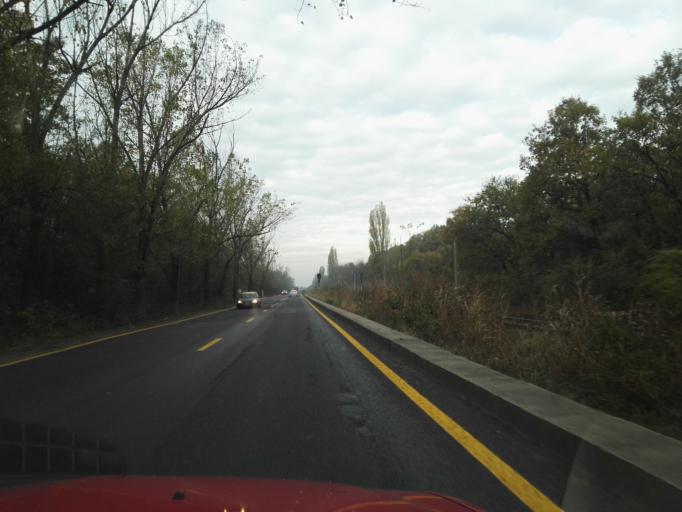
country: RO
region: Ilfov
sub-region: Comuna Magurele
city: Alunisu
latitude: 44.3545
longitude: 26.0511
